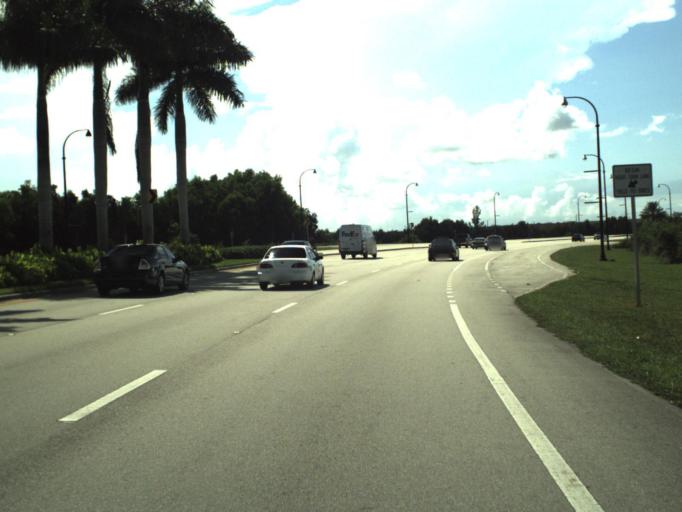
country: US
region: Florida
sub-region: Miami-Dade County
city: Country Club
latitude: 25.9830
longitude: -80.2970
